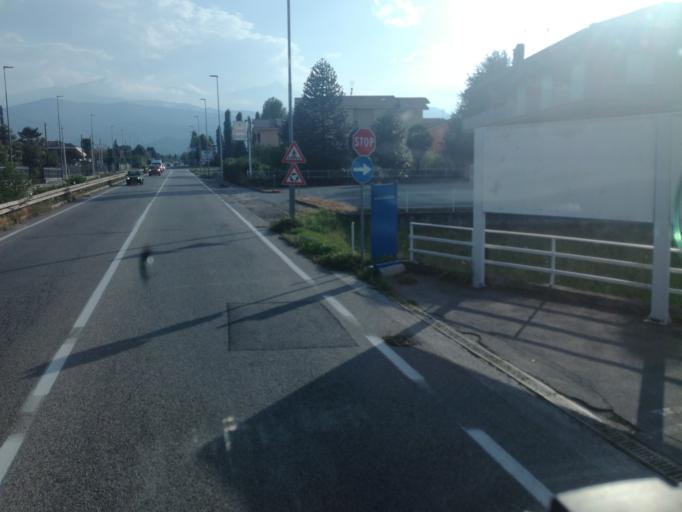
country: IT
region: Piedmont
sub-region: Provincia di Torino
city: Bricherasio
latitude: 44.8197
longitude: 7.3056
